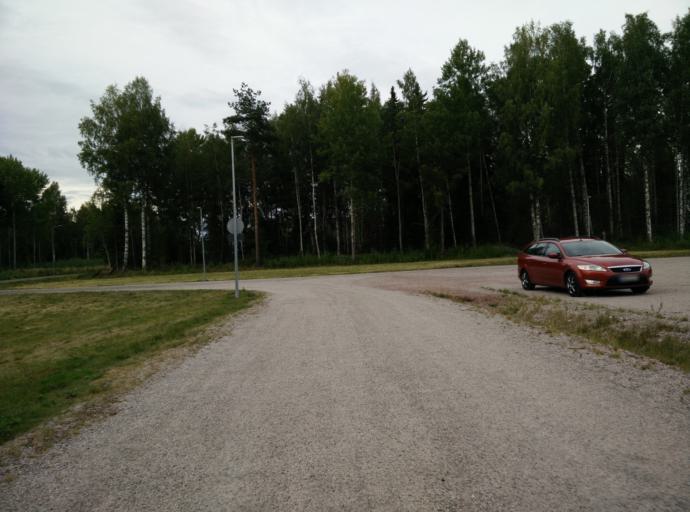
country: FI
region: Haeme
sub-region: Haemeenlinna
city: Haemeenlinna
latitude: 60.9857
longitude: 24.4806
